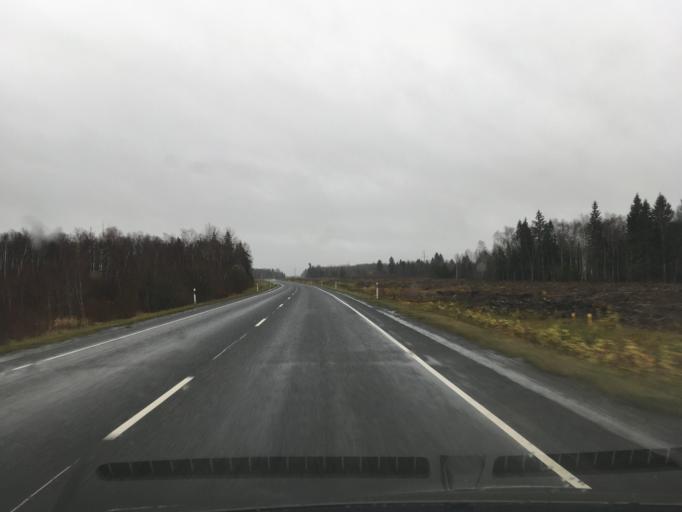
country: EE
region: Harju
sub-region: Nissi vald
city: Turba
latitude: 58.9449
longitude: 24.0856
